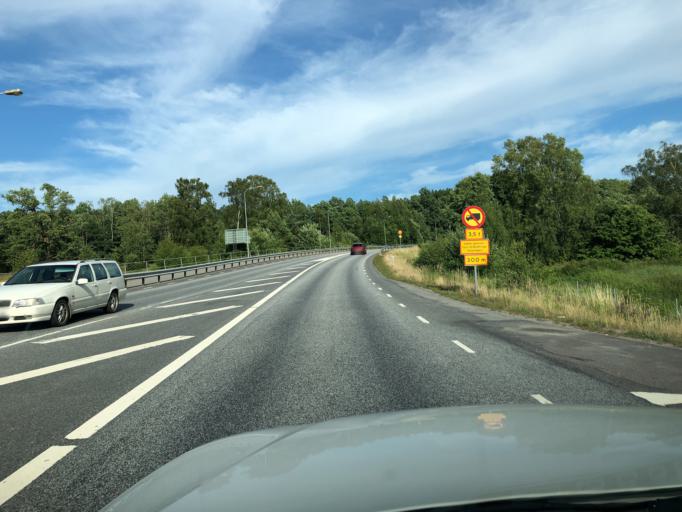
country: SE
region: Vaestra Goetaland
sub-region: Marks Kommun
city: Kinna
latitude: 57.4966
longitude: 12.6898
